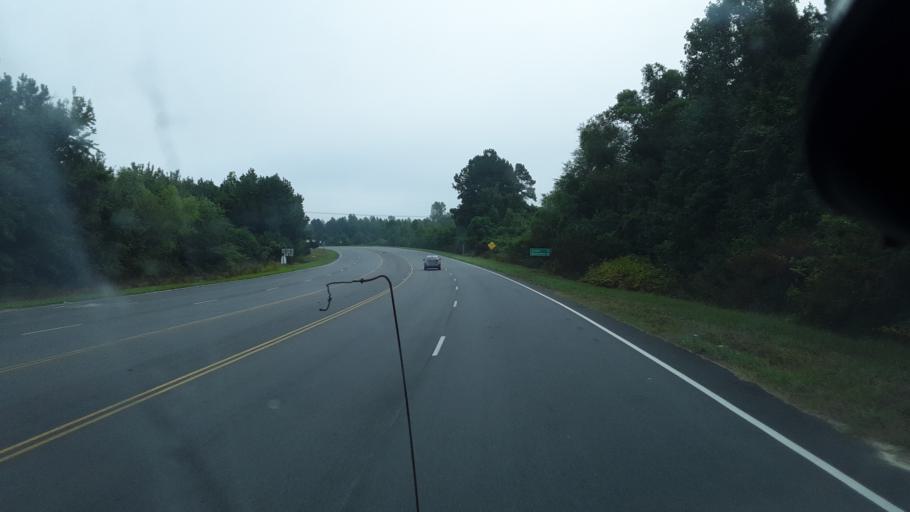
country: US
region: South Carolina
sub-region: Florence County
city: Johnsonville
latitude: 33.8833
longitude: -79.4519
